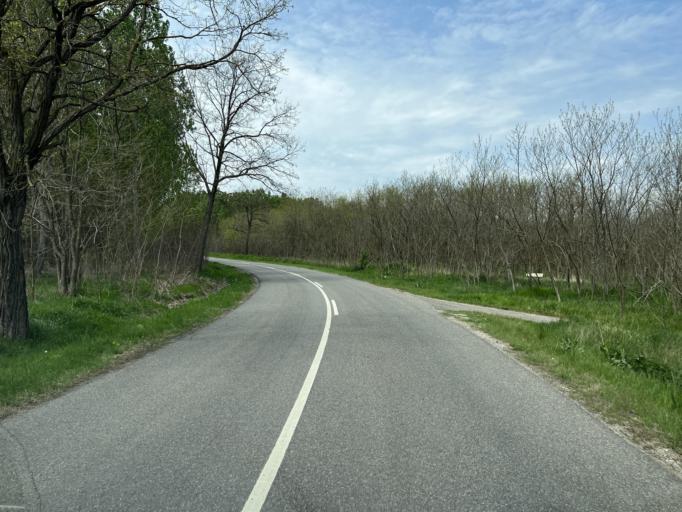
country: HU
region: Pest
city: Csemo
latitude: 47.1297
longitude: 19.6565
